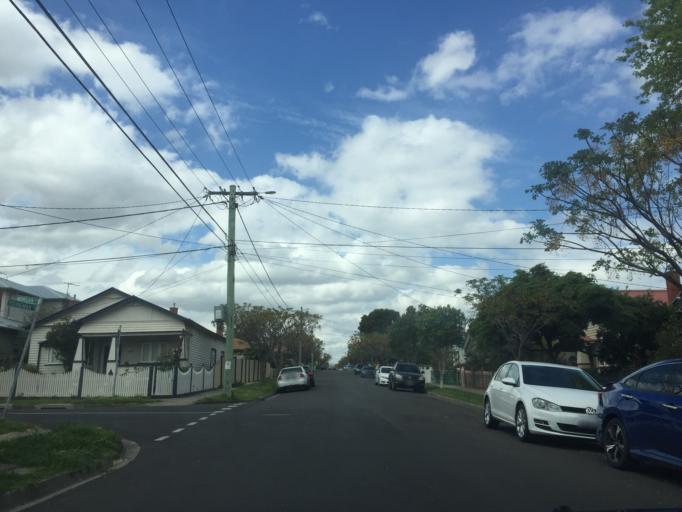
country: AU
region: Victoria
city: Thornbury
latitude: -37.7353
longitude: 145.0078
